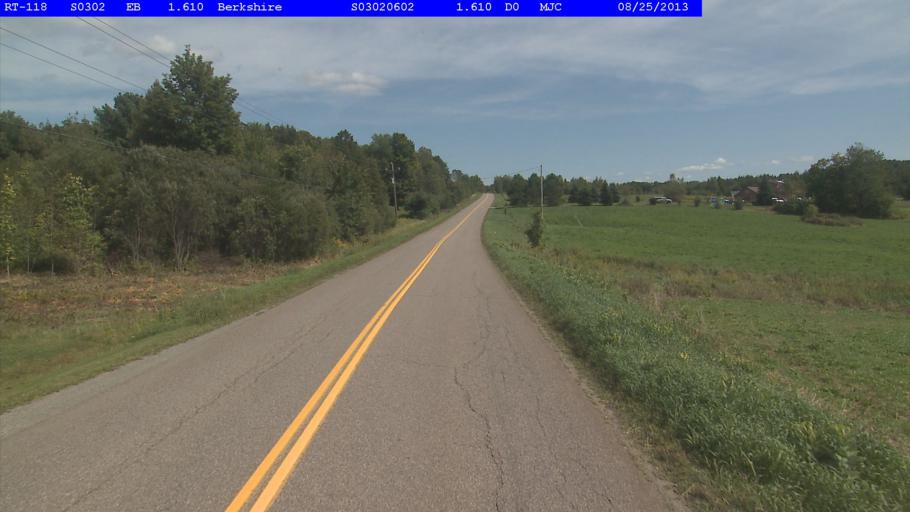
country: US
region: Vermont
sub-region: Franklin County
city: Enosburg Falls
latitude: 44.9794
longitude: -72.7848
